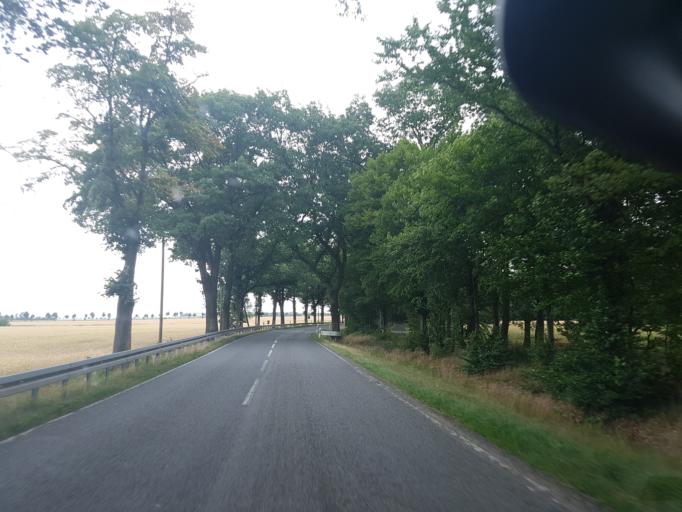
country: DE
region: Brandenburg
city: Dahme
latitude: 51.8487
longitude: 13.4108
